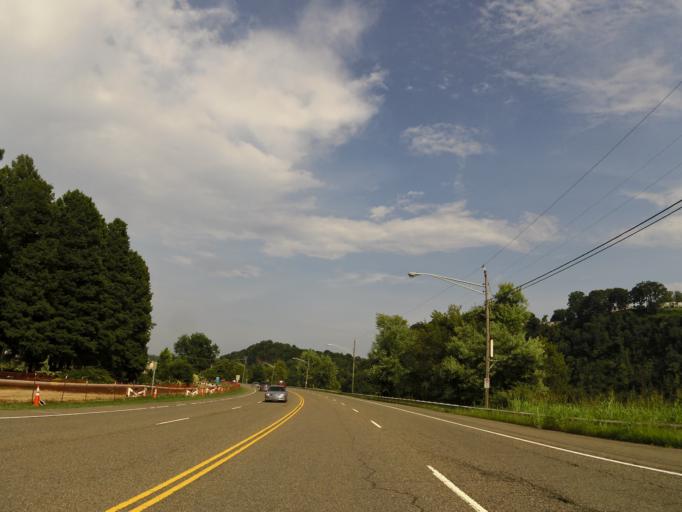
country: US
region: Tennessee
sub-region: Knox County
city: Knoxville
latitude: 35.9433
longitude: -83.9389
